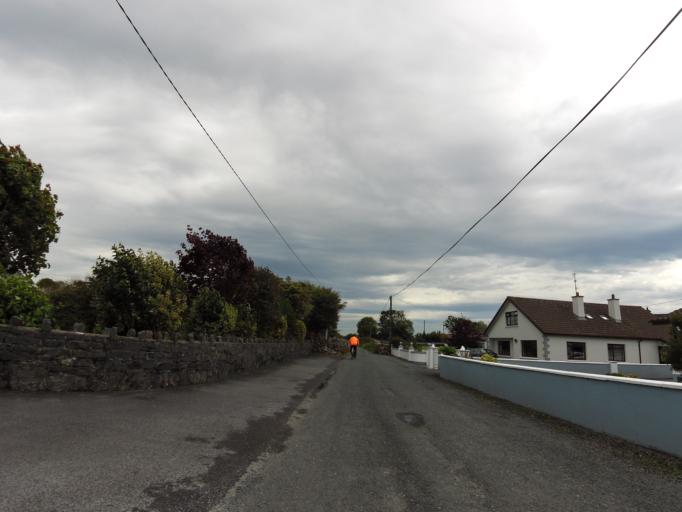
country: IE
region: Connaught
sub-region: County Galway
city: Gaillimh
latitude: 53.3157
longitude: -9.0436
